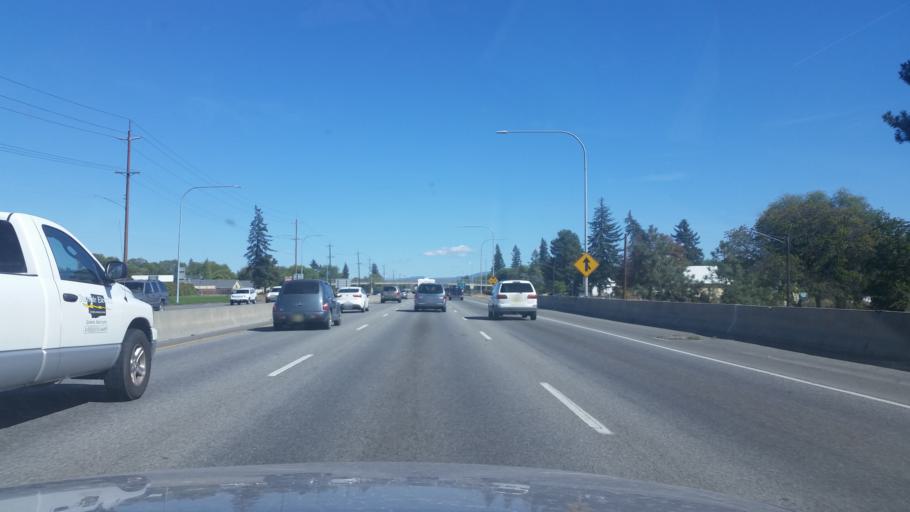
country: US
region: Washington
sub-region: Spokane County
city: Spokane
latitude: 47.6539
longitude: -117.3729
